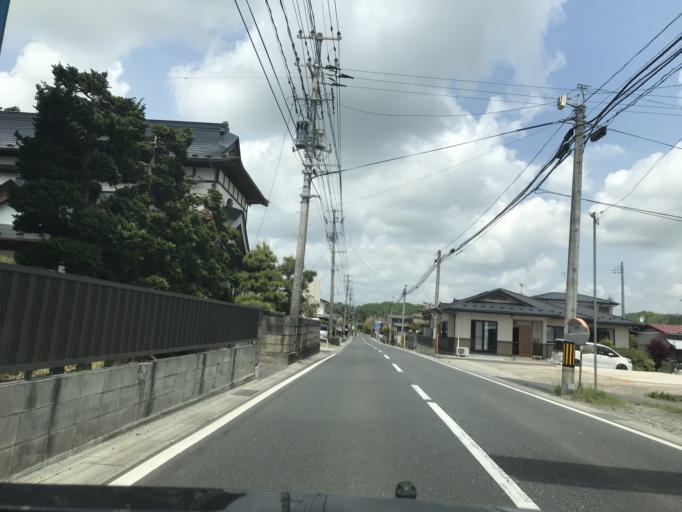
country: JP
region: Miyagi
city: Kogota
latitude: 38.6627
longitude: 141.0666
